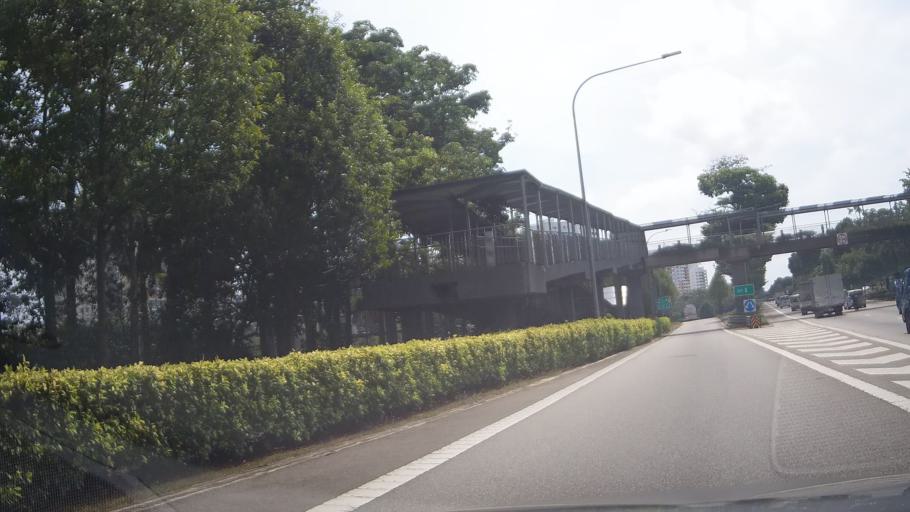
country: SG
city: Singapore
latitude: 1.3357
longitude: 103.9305
